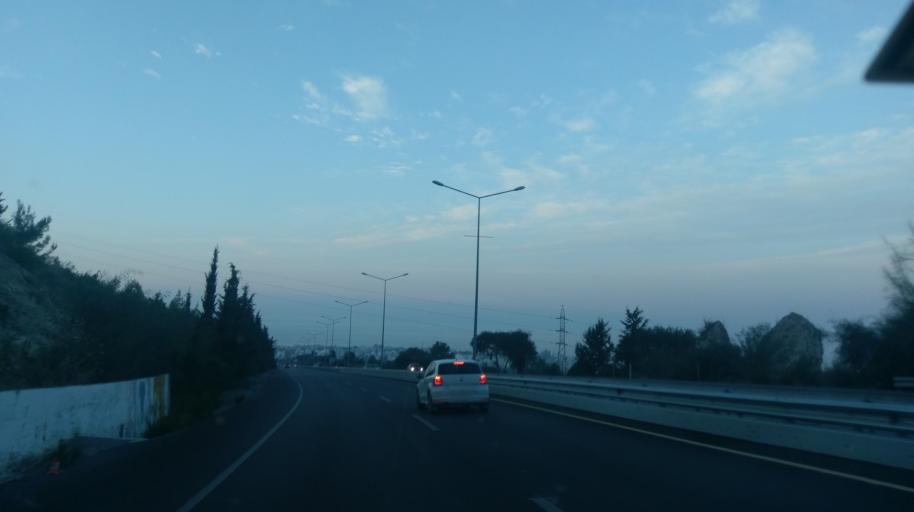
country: CY
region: Keryneia
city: Kyrenia
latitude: 35.3127
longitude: 33.3239
